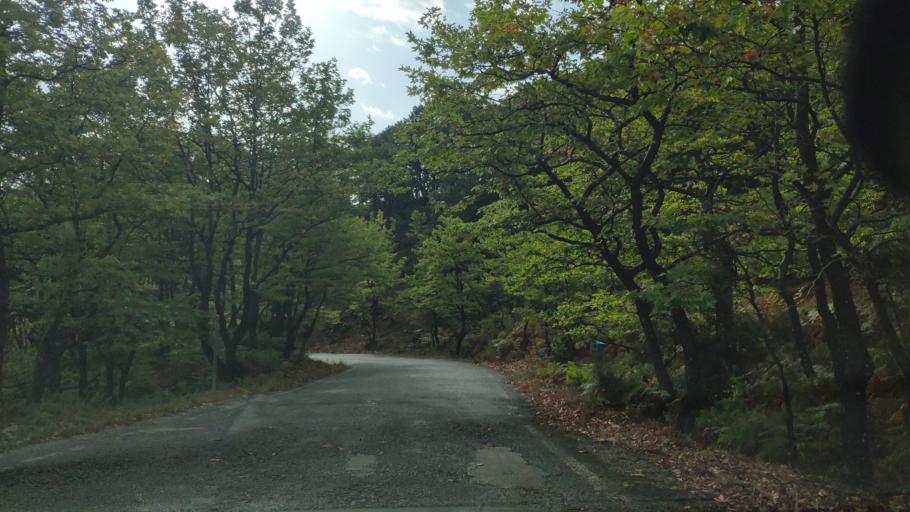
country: GR
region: West Greece
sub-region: Nomos Aitolias kai Akarnanias
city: Sardinia
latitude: 38.8648
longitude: 21.2981
